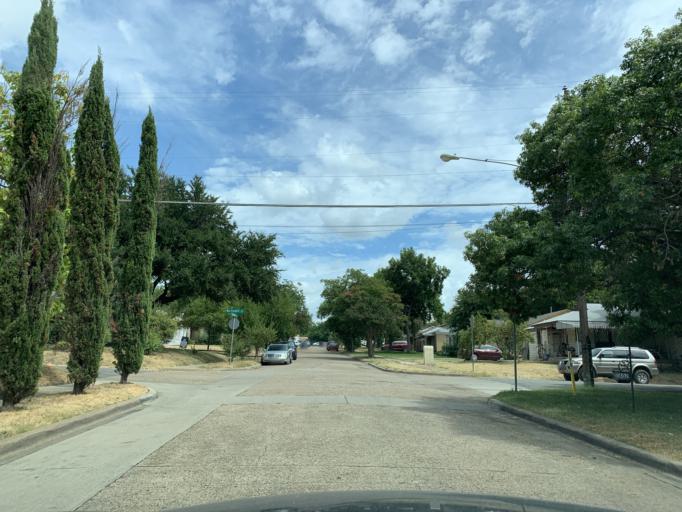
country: US
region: Texas
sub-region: Dallas County
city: Cockrell Hill
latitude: 32.7359
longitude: -96.8763
